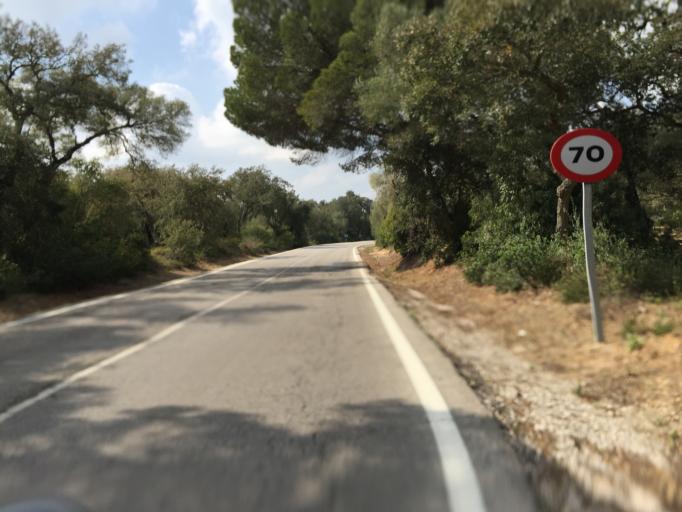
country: ES
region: Andalusia
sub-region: Provincia de Cadiz
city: Vejer de la Frontera
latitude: 36.3005
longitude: -5.9096
